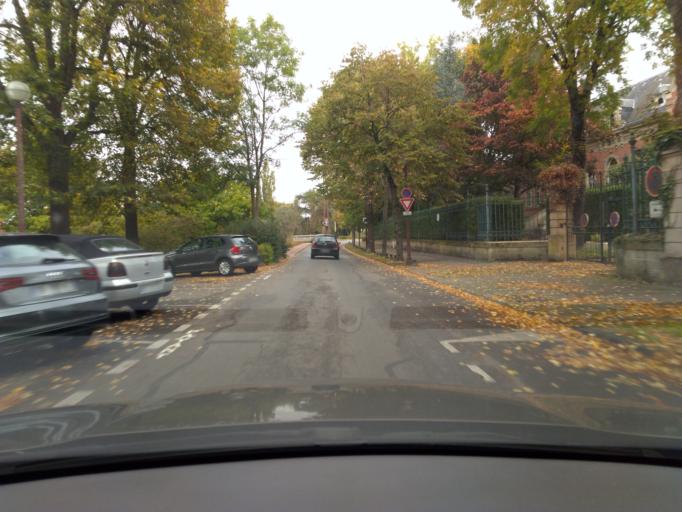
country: FR
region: Lorraine
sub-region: Departement de la Moselle
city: Metz
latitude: 49.1119
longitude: 6.1656
